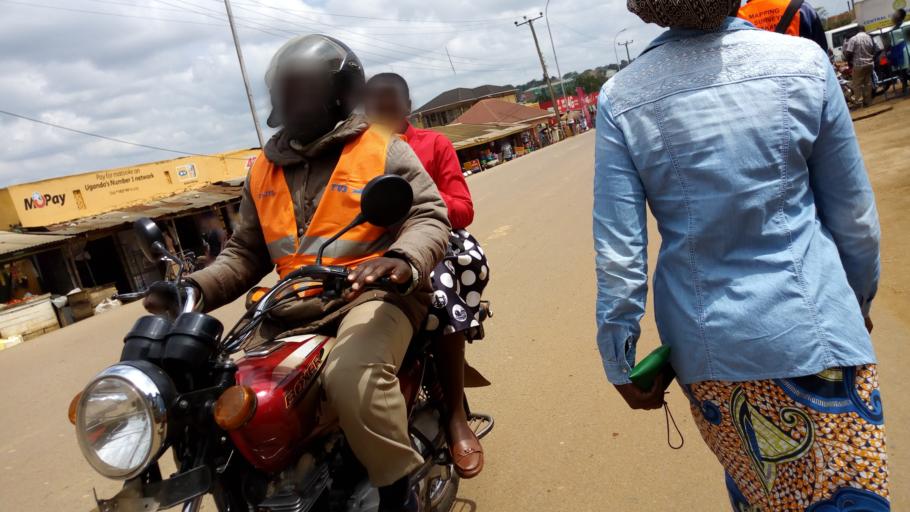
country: UG
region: Central Region
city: Kampala Central Division
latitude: 0.3810
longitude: 32.5595
